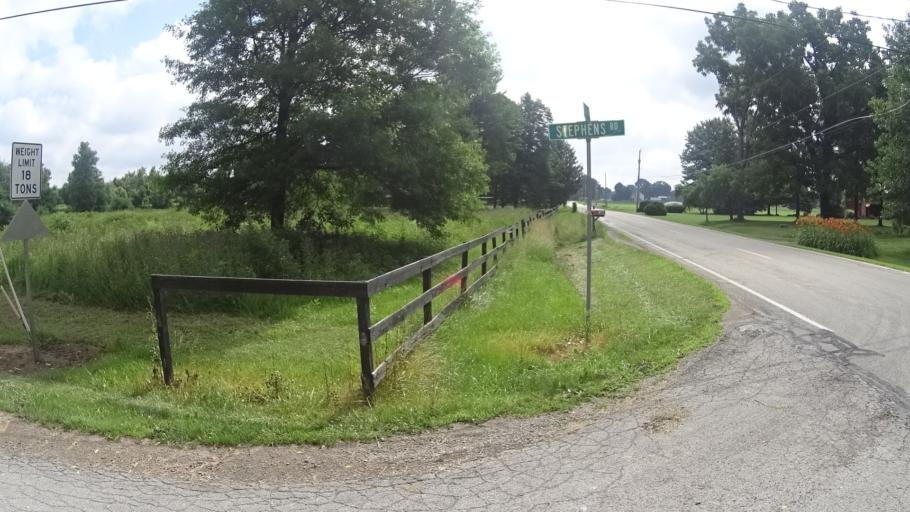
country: US
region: Ohio
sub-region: Huron County
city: Wakeman
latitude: 41.3257
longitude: -82.4386
